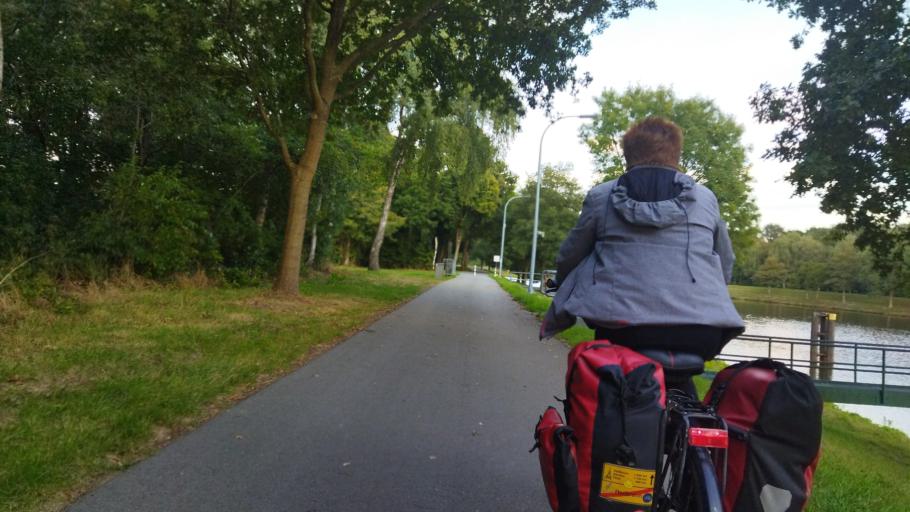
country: DE
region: Lower Saxony
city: Heede
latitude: 52.9864
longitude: 7.3164
